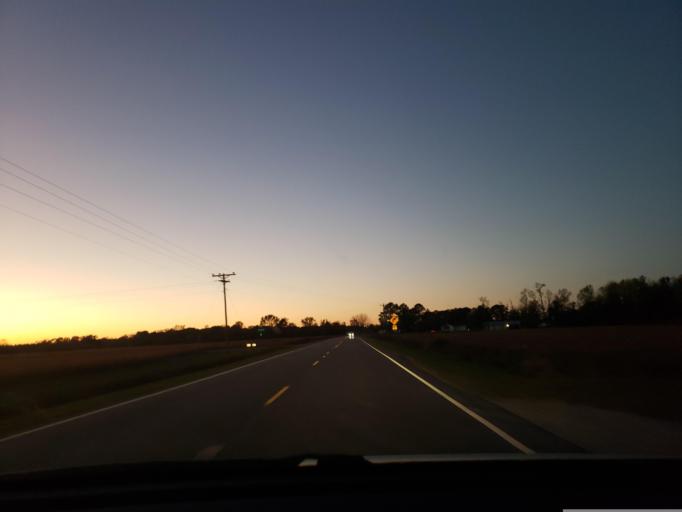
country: US
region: North Carolina
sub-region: Duplin County
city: Kenansville
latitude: 34.9085
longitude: -77.9260
